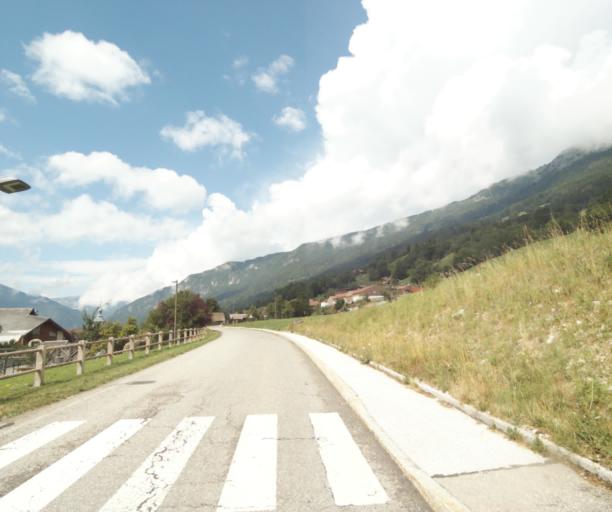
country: FR
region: Rhone-Alpes
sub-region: Departement de la Haute-Savoie
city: Saint-Jean-de-Sixt
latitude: 45.9084
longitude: 6.3671
